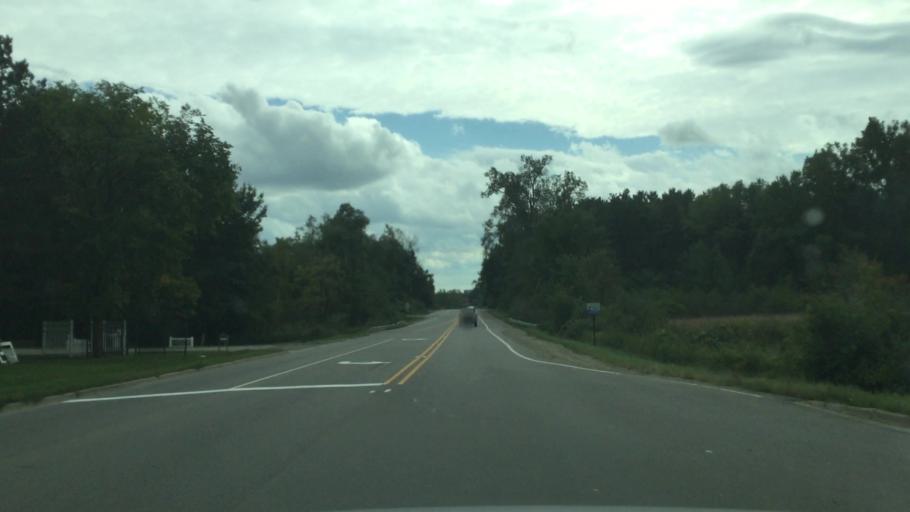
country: US
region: Michigan
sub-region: Livingston County
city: Brighton
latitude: 42.5523
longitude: -83.7529
